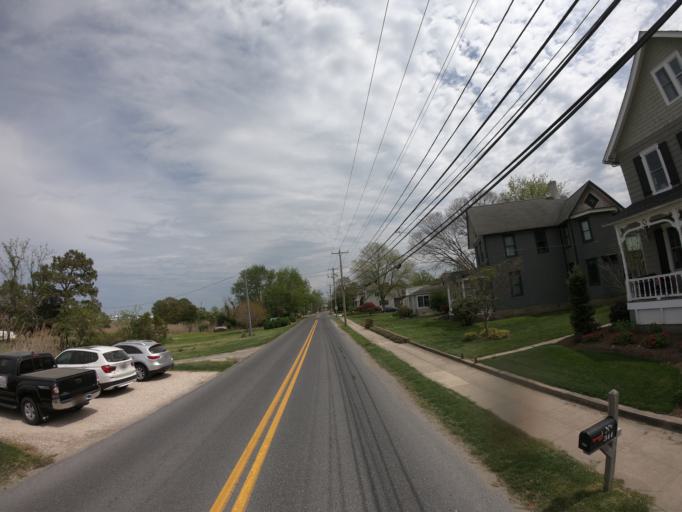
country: US
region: Delaware
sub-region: Sussex County
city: Lewes
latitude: 38.7784
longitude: -75.1455
